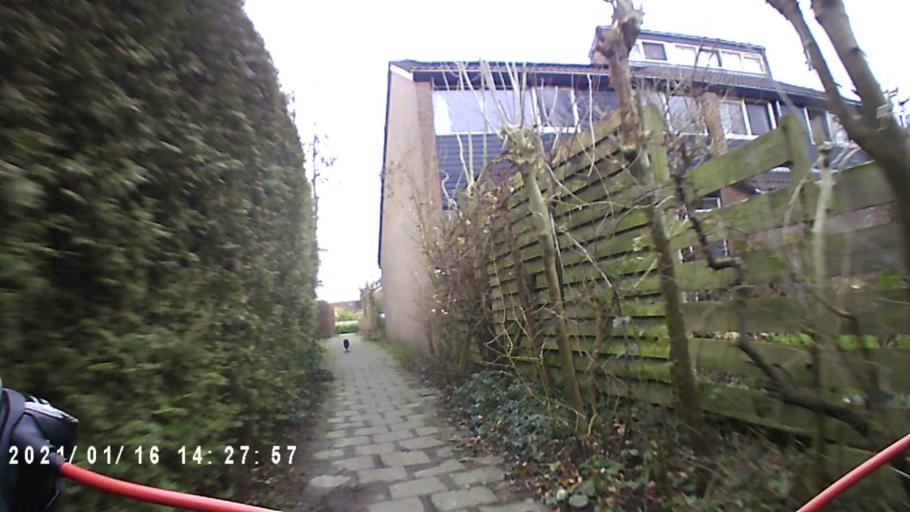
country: NL
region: Groningen
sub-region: Gemeente Winsum
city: Winsum
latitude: 53.3263
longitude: 6.5266
